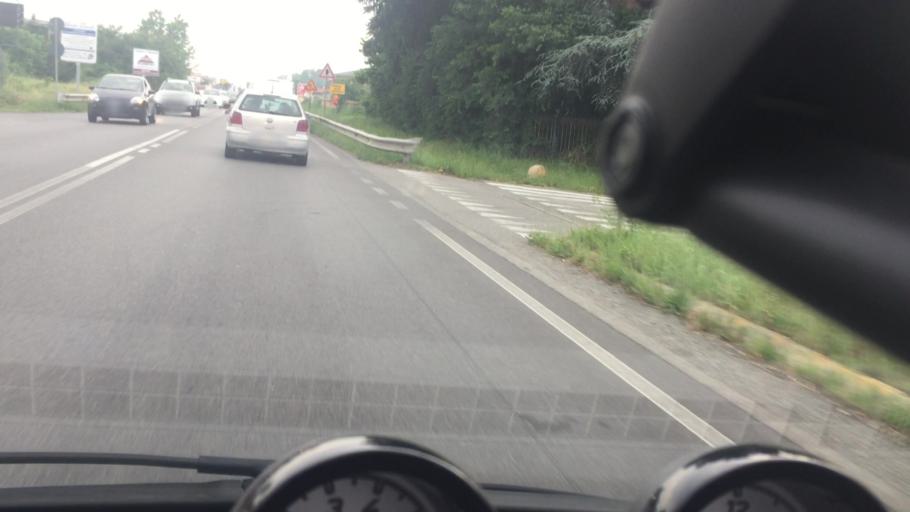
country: IT
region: Lombardy
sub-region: Provincia di Bergamo
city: Osio Sotto
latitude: 45.6124
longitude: 9.5915
